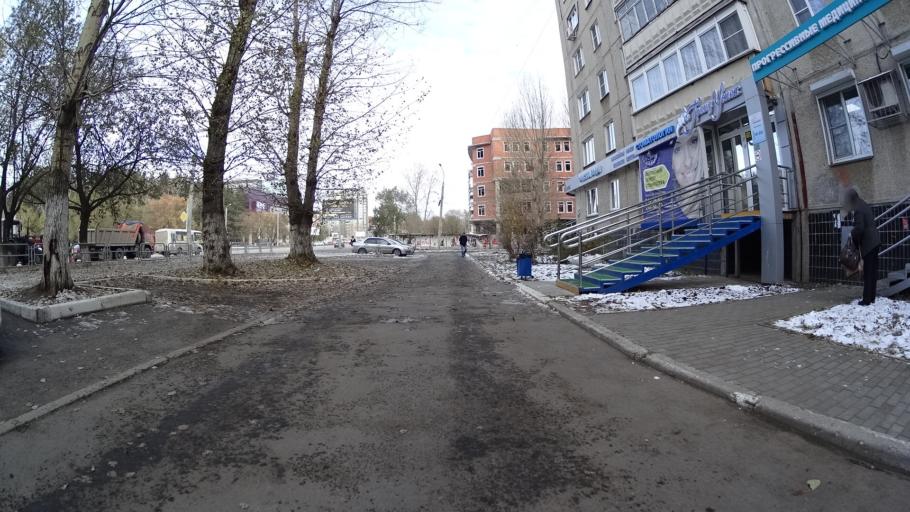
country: RU
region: Chelyabinsk
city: Roshchino
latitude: 55.1914
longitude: 61.2974
